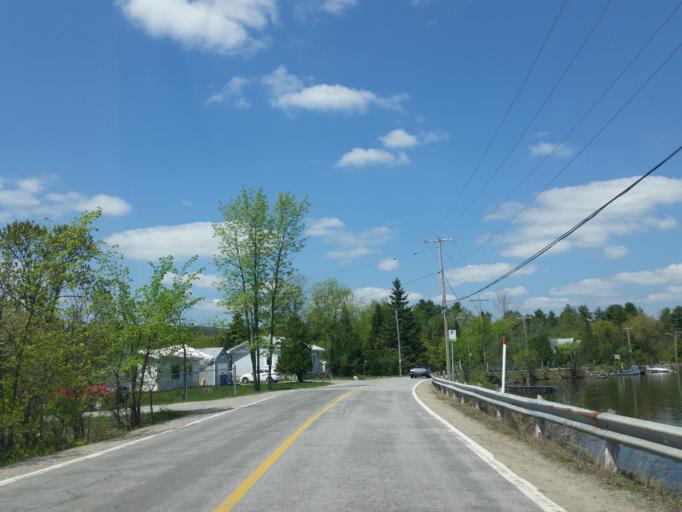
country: CA
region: Quebec
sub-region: Outaouais
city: Wakefield
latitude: 45.6026
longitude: -75.8881
